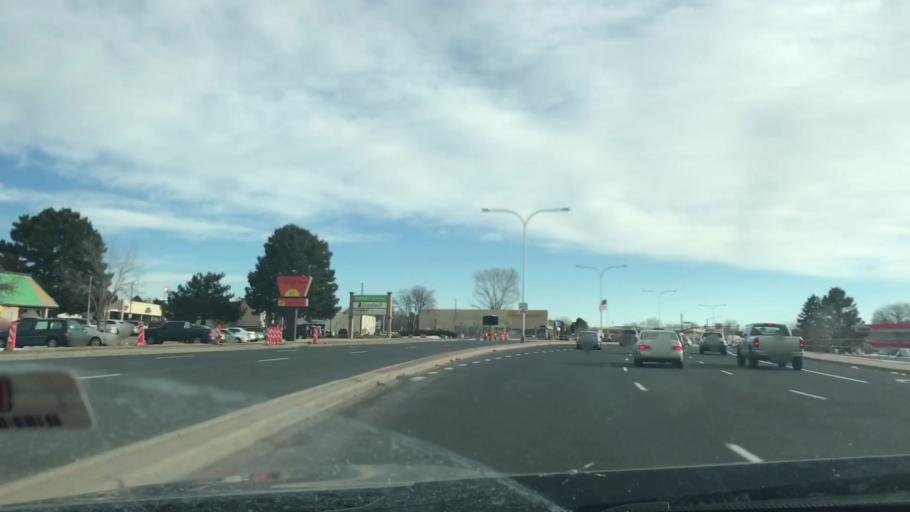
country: US
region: Colorado
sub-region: El Paso County
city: Cimarron Hills
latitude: 38.8939
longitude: -104.7576
